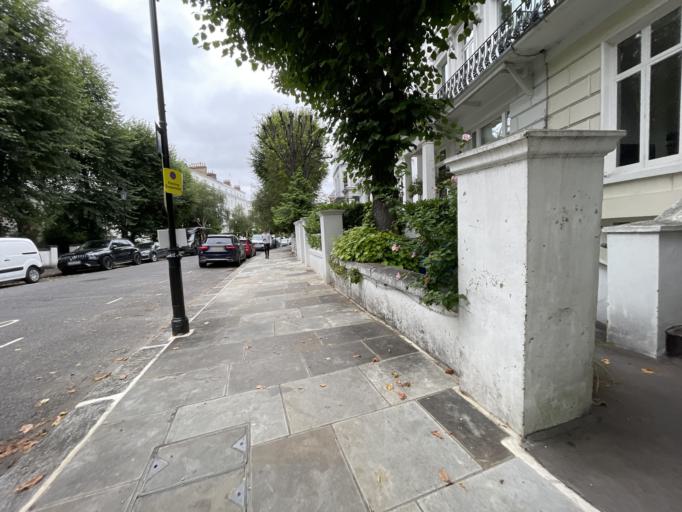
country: GB
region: England
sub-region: Greater London
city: Kensington
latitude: 51.5120
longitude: -0.1990
